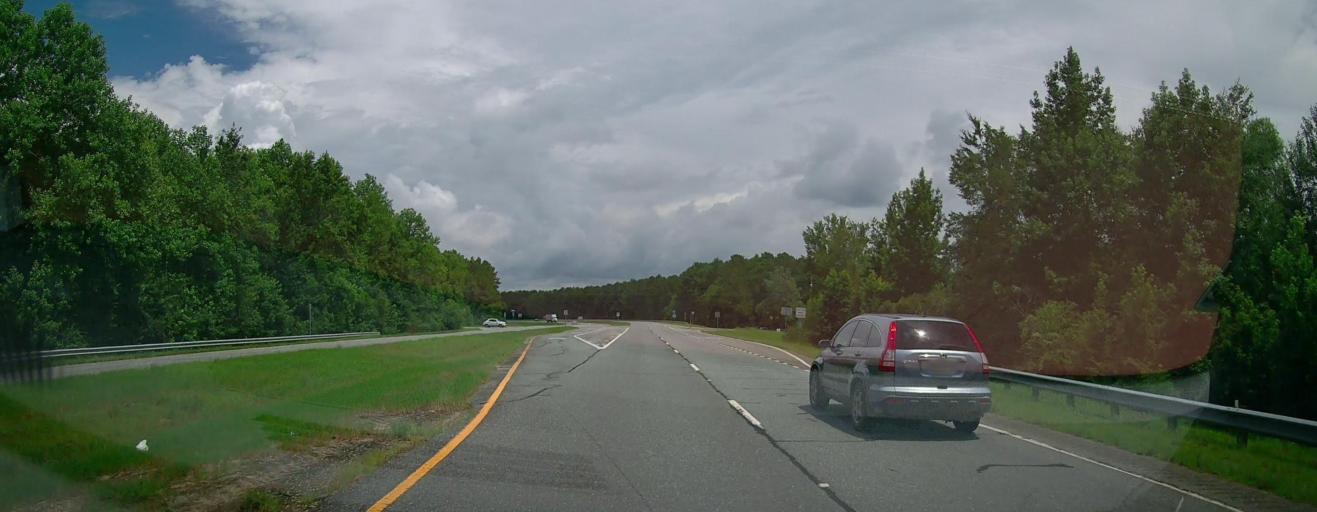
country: US
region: Georgia
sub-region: Dodge County
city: Eastman
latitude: 32.1816
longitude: -83.1936
